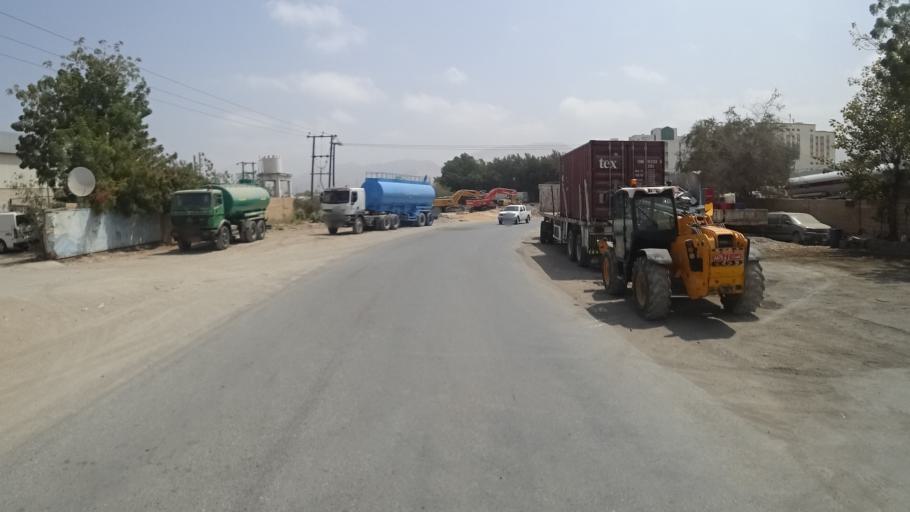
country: OM
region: Muhafazat Masqat
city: Bawshar
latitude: 23.5759
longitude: 58.3743
